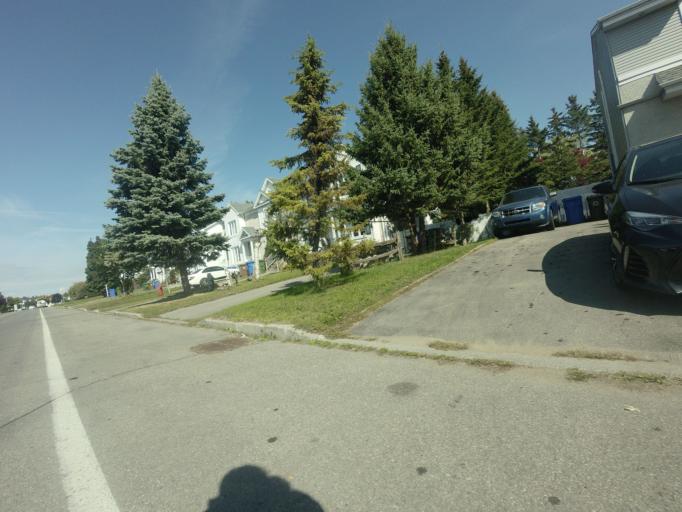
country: CA
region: Quebec
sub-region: Laurentides
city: Saint-Eustache
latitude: 45.5733
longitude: -73.9223
